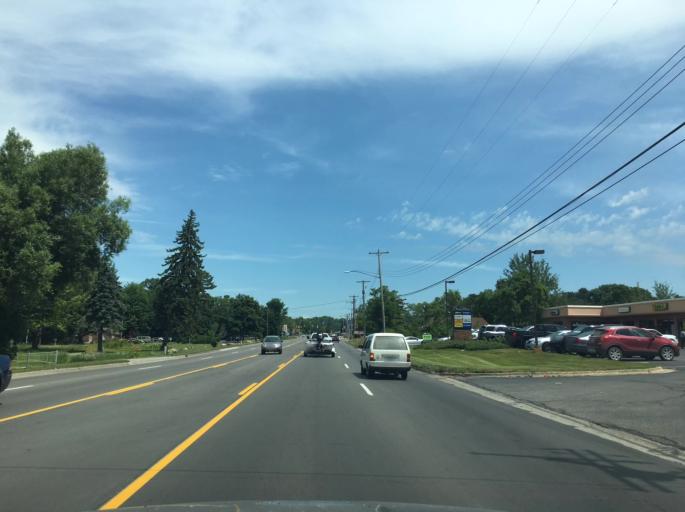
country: US
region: Michigan
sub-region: Grand Traverse County
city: Traverse City
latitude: 44.7705
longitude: -85.5029
